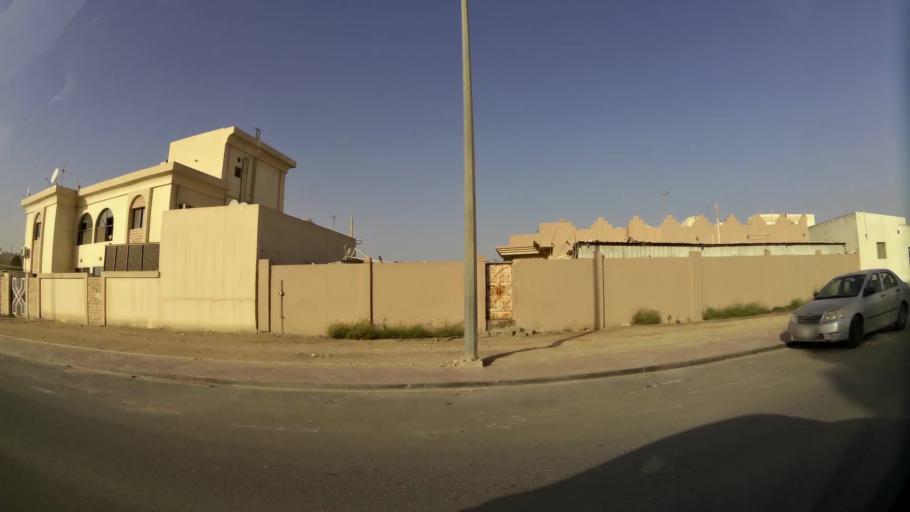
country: QA
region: Baladiyat ar Rayyan
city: Ar Rayyan
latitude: 25.3386
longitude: 51.4540
